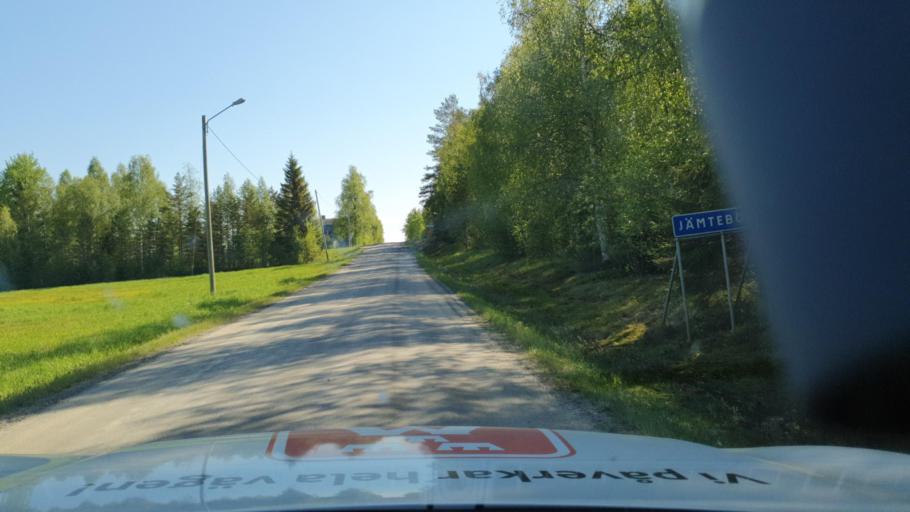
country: SE
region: Vaesterbotten
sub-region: Vannas Kommun
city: Vaennaes
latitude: 63.9928
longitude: 19.7651
